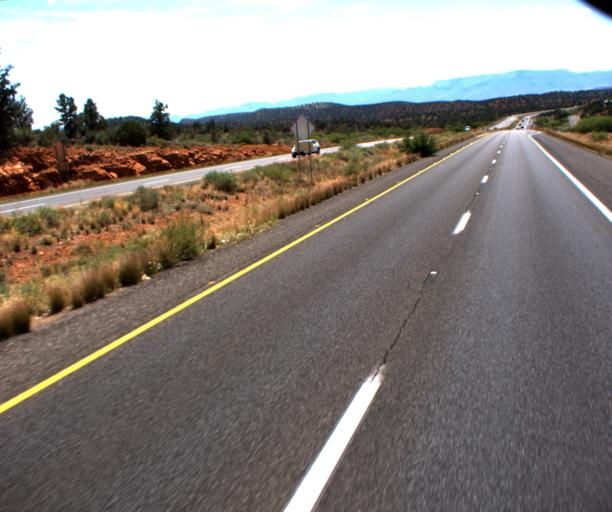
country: US
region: Arizona
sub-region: Yavapai County
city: West Sedona
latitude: 34.8450
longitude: -111.8594
